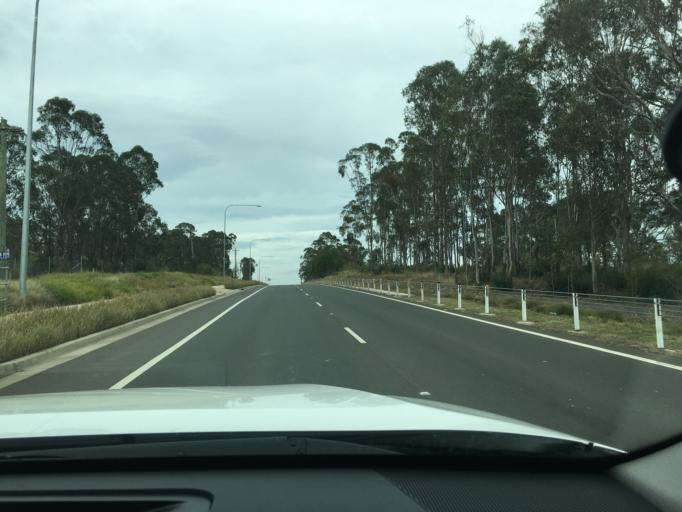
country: AU
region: New South Wales
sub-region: Campbelltown Municipality
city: Denham Court
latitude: -33.9873
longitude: 150.7931
